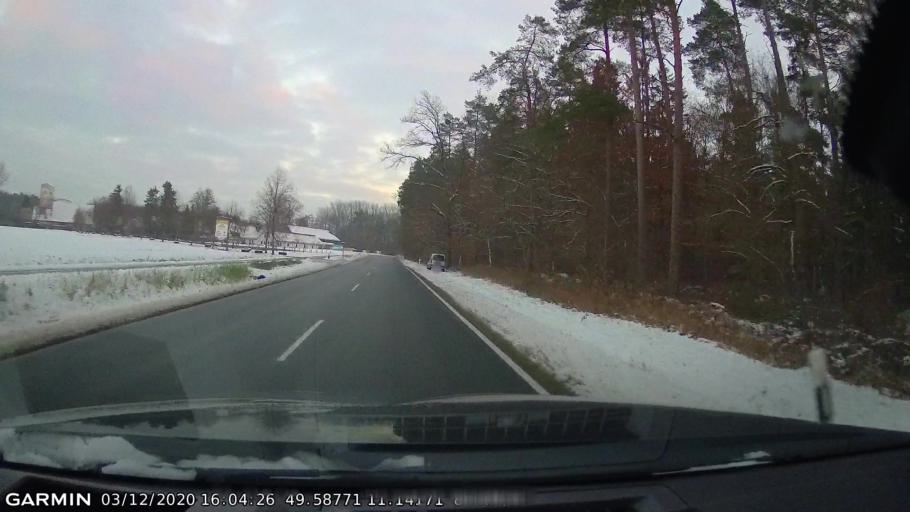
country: DE
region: Bavaria
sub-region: Upper Franconia
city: Kleinsendelbach
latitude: 49.5877
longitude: 11.1418
